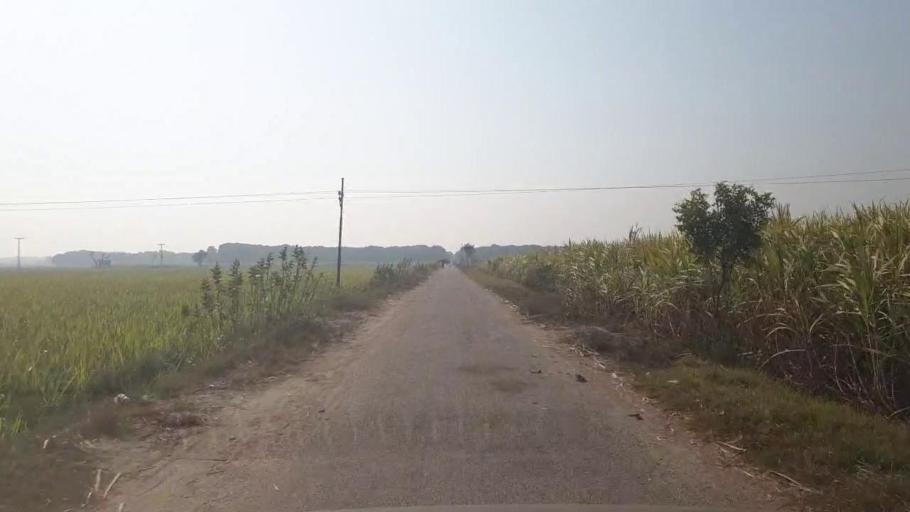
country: PK
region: Sindh
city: Tando Allahyar
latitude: 25.4756
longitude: 68.7615
